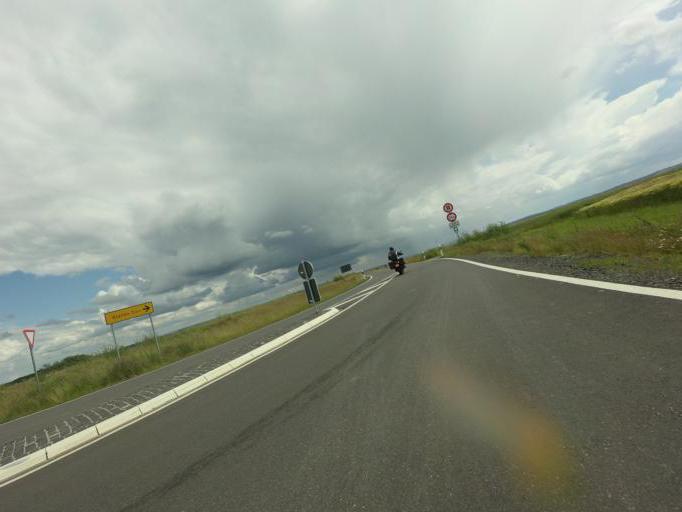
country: DE
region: Rheinland-Pfalz
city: Wirfus
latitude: 50.1901
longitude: 7.2019
